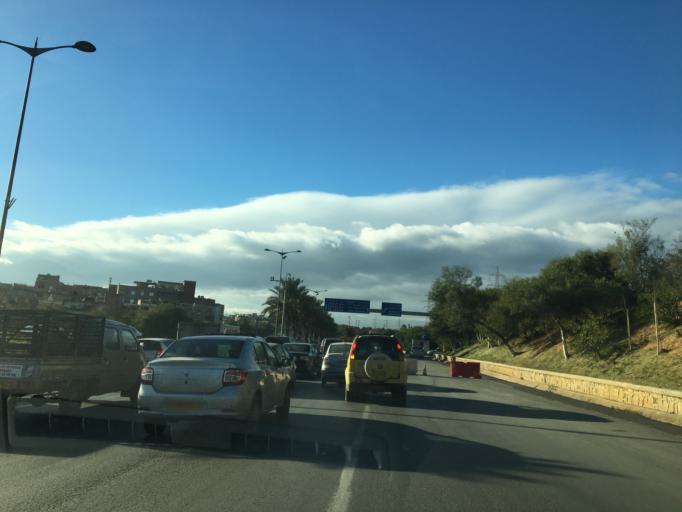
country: DZ
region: Tipaza
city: Baraki
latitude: 36.7086
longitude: 3.1080
